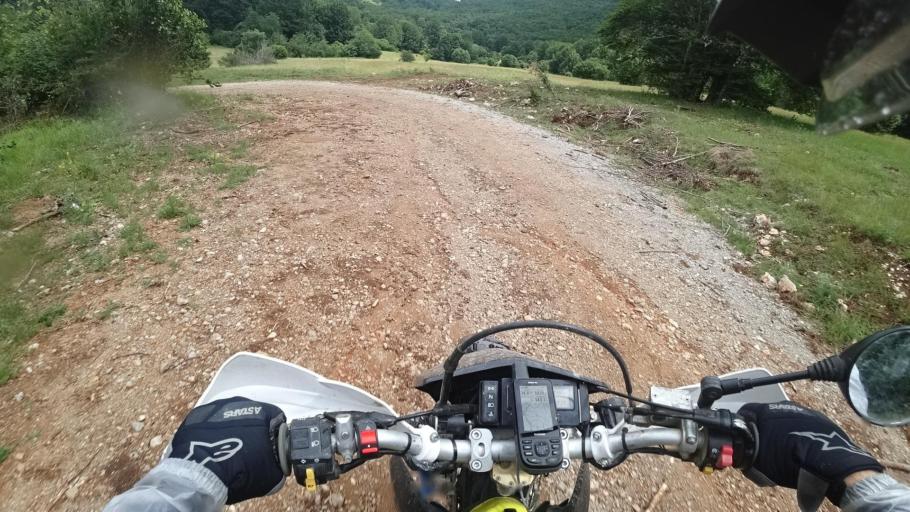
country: BA
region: Federation of Bosnia and Herzegovina
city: Bihac
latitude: 44.6516
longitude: 15.7708
